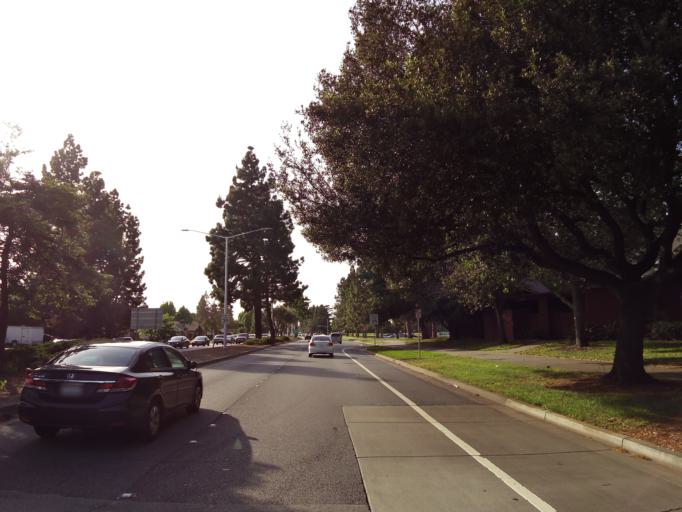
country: US
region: California
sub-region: Alameda County
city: Fremont
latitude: 37.5459
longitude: -121.9666
